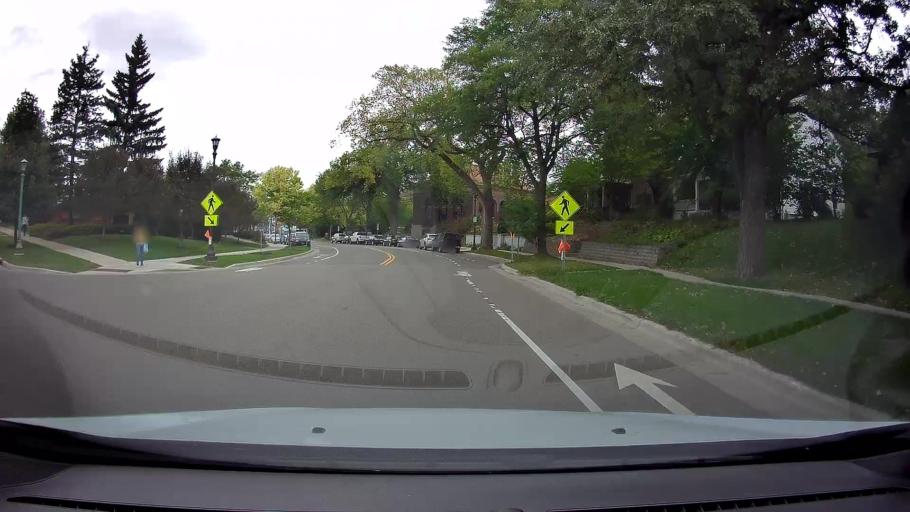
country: US
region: Minnesota
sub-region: Ramsey County
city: Lauderdale
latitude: 44.9802
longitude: -93.1936
